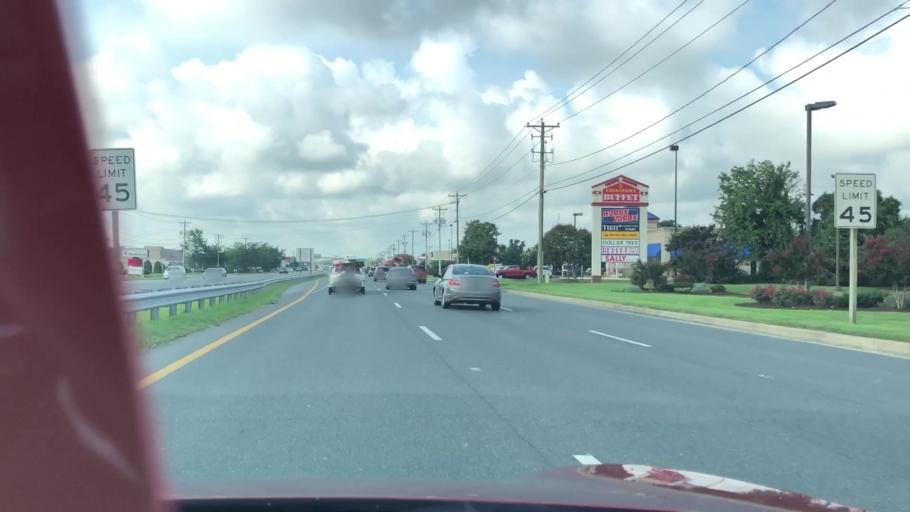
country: US
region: Maryland
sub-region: Wicomico County
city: Delmar
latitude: 38.4205
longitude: -75.5634
